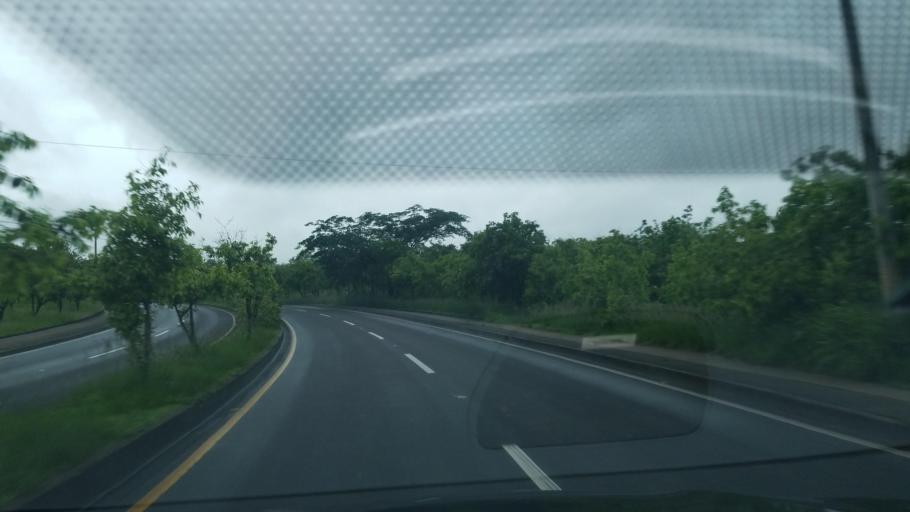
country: HN
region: Francisco Morazan
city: Yaguacire
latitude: 14.0468
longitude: -87.2240
